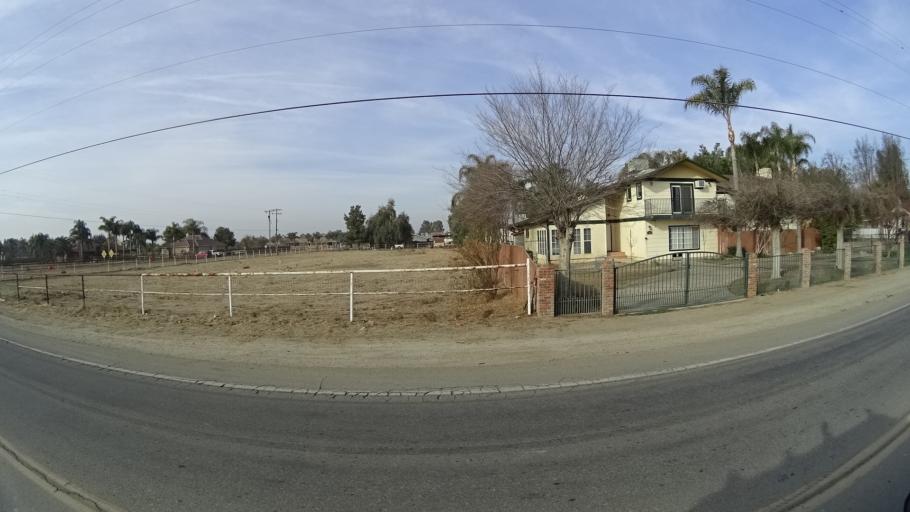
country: US
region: California
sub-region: Kern County
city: Lamont
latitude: 35.3253
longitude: -118.9319
